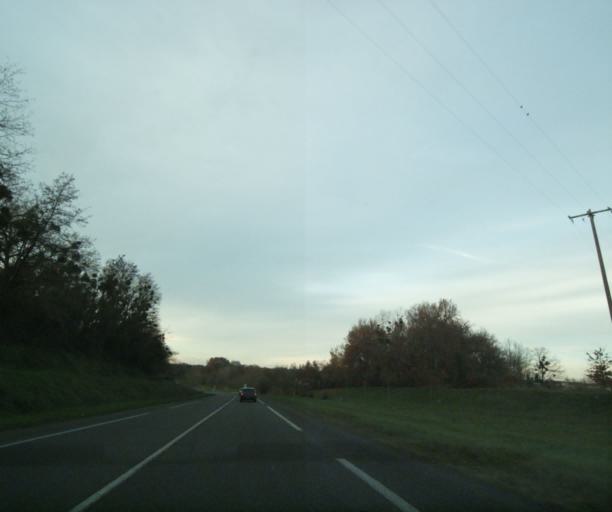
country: FR
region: Aquitaine
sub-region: Departement de la Gironde
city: Bazas
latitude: 44.4268
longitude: -0.2293
